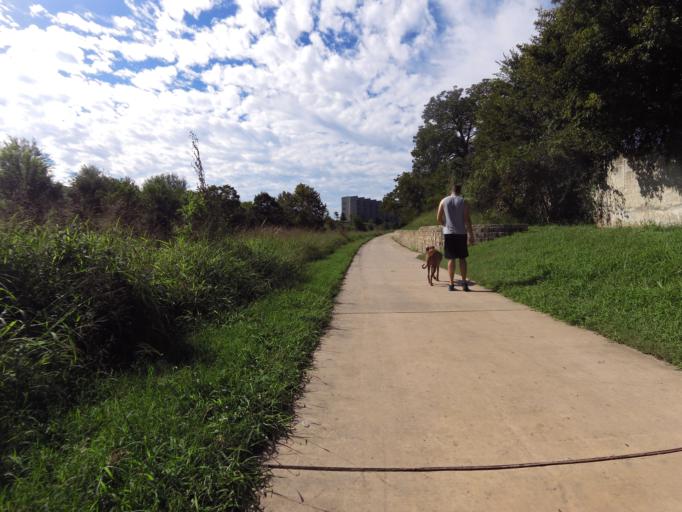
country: US
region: Texas
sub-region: Bexar County
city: San Antonio
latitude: 29.4034
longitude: -98.4879
